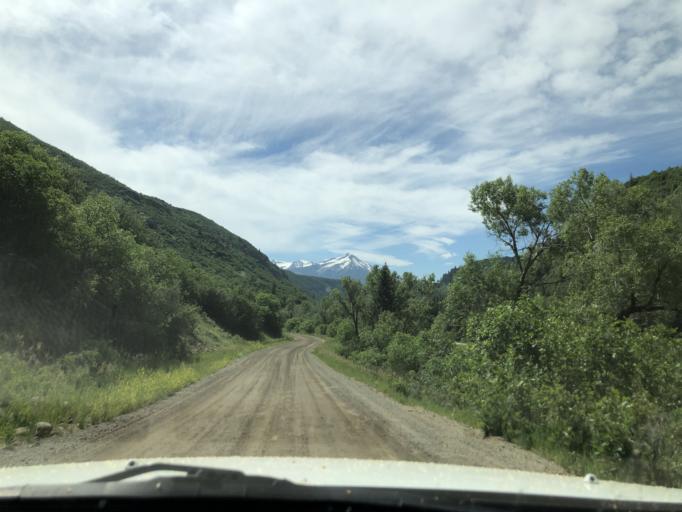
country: US
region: Colorado
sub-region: Delta County
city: Paonia
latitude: 38.9921
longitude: -107.3503
